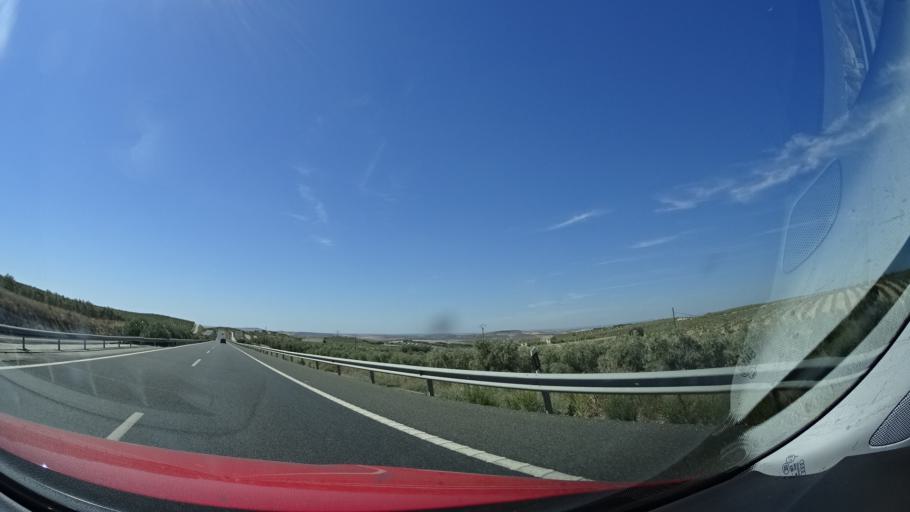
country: ES
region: Andalusia
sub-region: Provincia de Sevilla
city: Gilena
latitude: 37.2780
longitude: -4.9329
